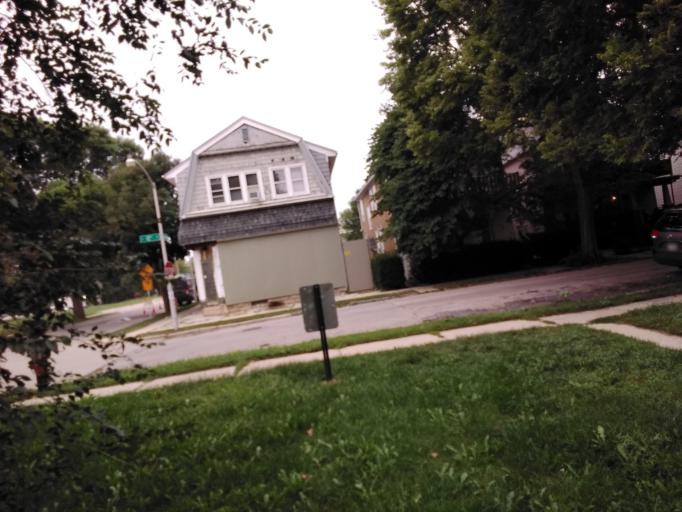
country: US
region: Wisconsin
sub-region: Milwaukee County
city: Milwaukee
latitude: 42.9978
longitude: -87.9271
